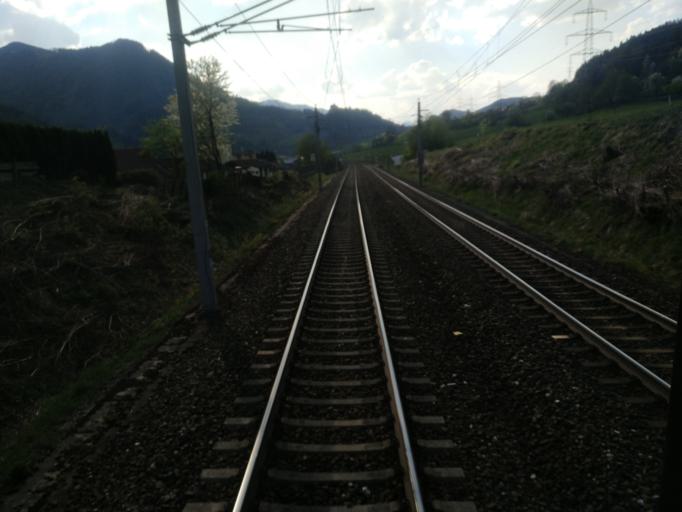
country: AT
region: Styria
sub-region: Politischer Bezirk Liezen
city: Rottenmann
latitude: 47.5277
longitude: 14.3483
